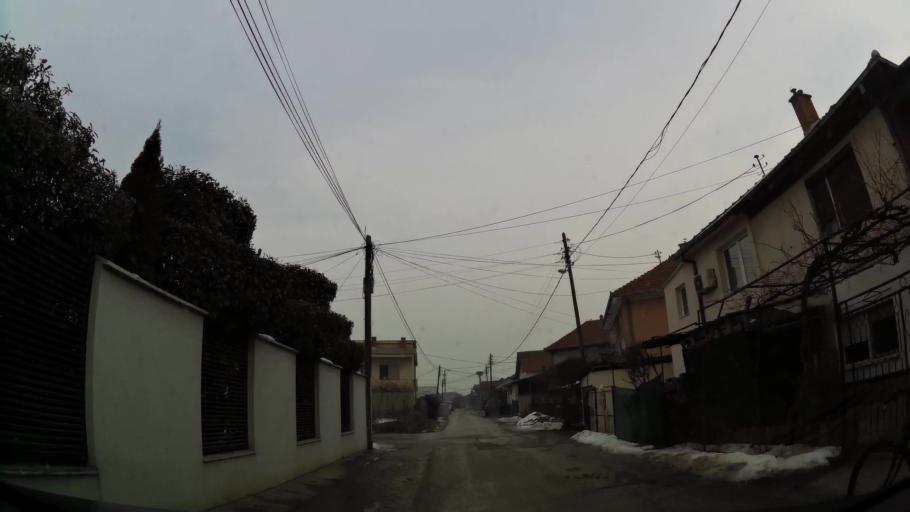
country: MK
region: Ilinden
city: Jurumleri
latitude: 41.9676
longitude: 21.5614
